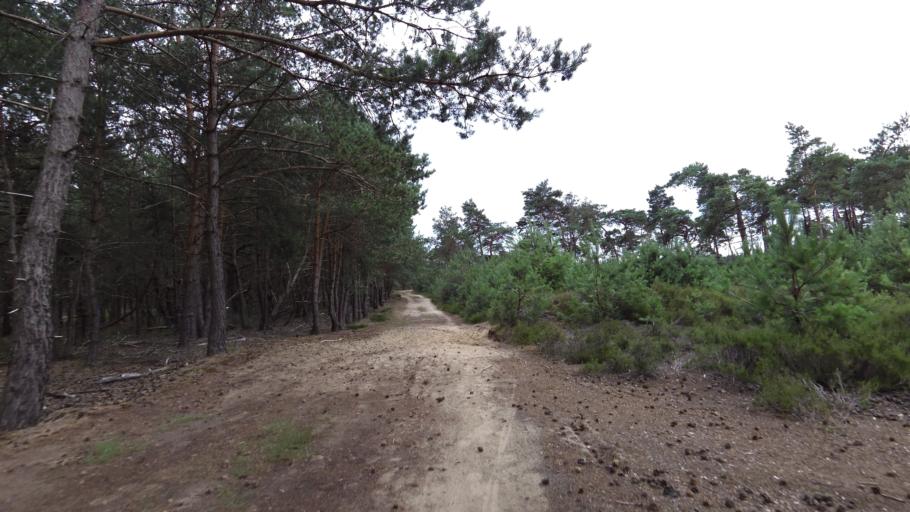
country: NL
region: Gelderland
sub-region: Gemeente Apeldoorn
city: Uddel
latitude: 52.2298
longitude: 5.8024
